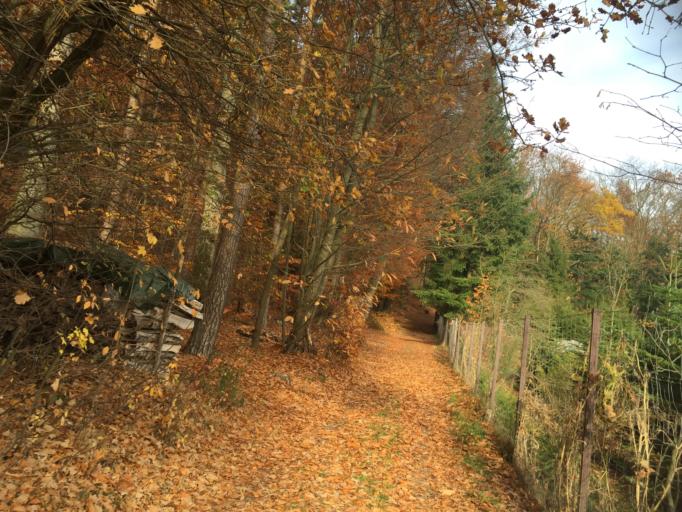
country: DE
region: Rheinland-Pfalz
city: Altleiningen
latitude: 49.4909
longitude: 8.0728
